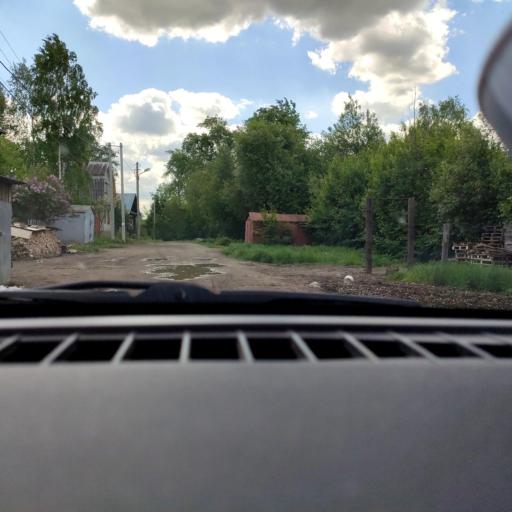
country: RU
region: Perm
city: Perm
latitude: 58.0202
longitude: 56.3272
